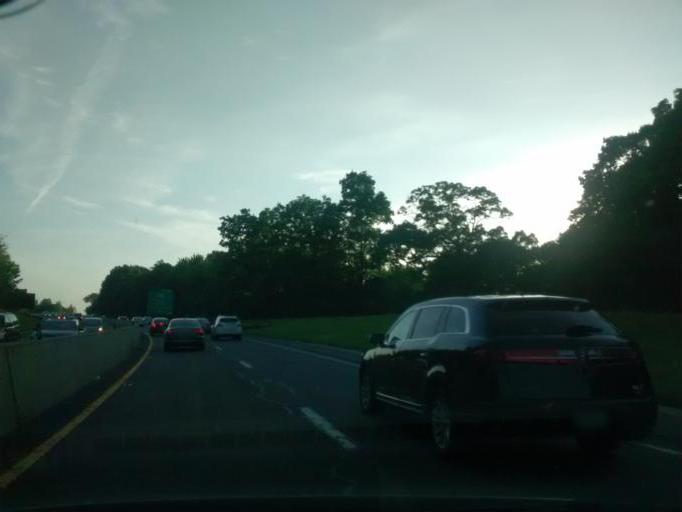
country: US
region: New York
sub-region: Westchester County
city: Purchase
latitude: 41.0245
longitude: -73.7040
